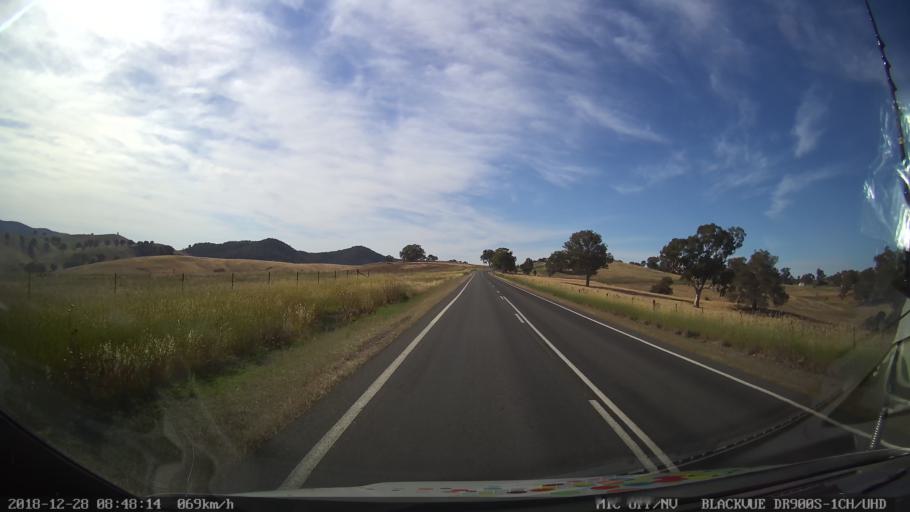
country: AU
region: New South Wales
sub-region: Upper Lachlan Shire
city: Crookwell
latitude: -34.0345
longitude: 149.3365
